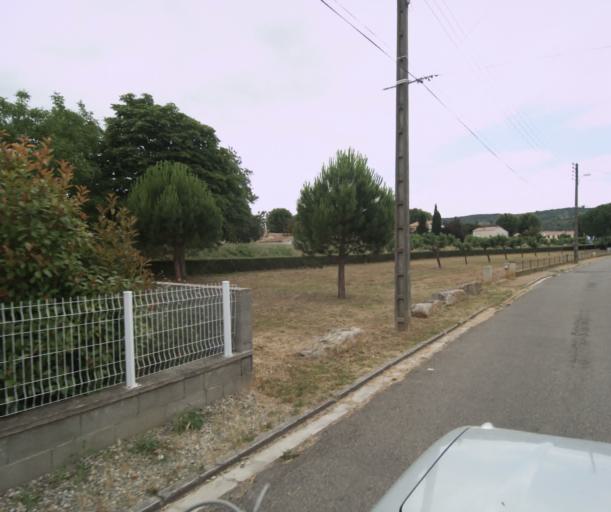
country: FR
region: Languedoc-Roussillon
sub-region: Departement de l'Aude
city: Limoux
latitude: 43.0659
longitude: 2.2185
